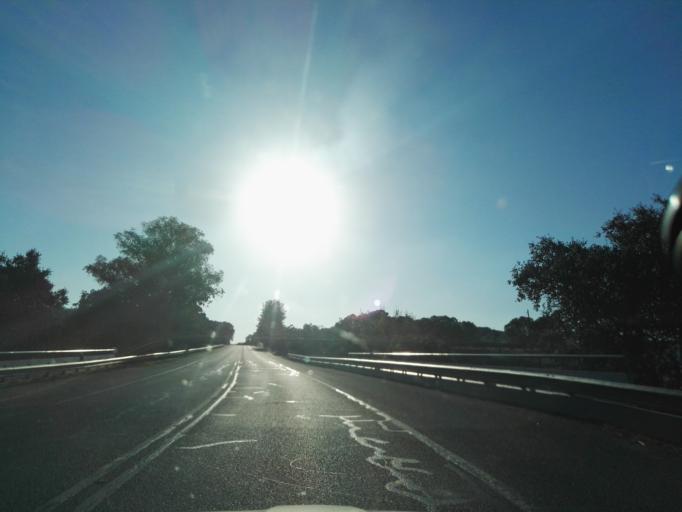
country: PT
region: Evora
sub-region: Vila Vicosa
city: Vila Vicosa
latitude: 38.8397
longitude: -7.3971
